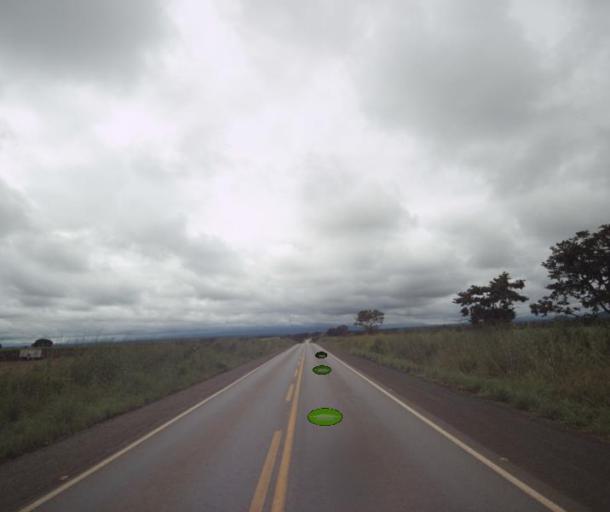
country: BR
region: Goias
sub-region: Uruacu
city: Uruacu
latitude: -14.7143
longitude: -49.0892
